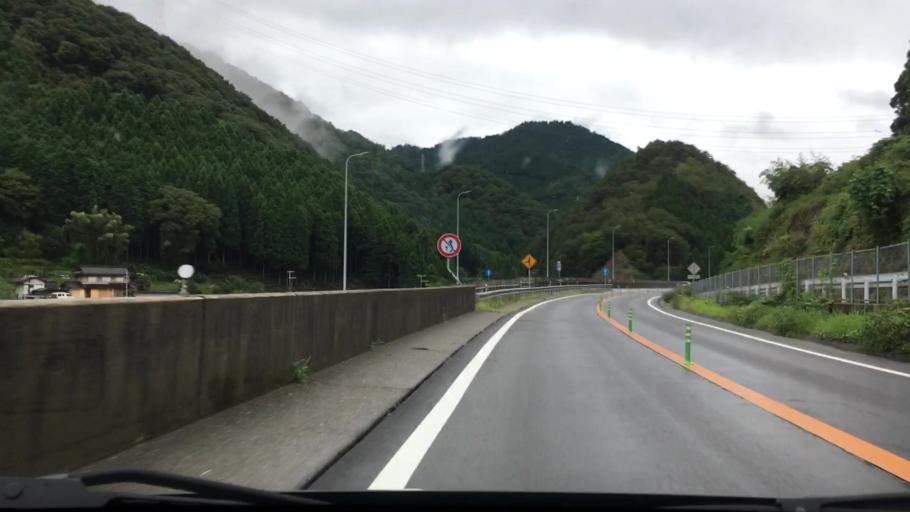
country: JP
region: Hyogo
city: Nishiwaki
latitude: 35.1882
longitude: 134.7915
